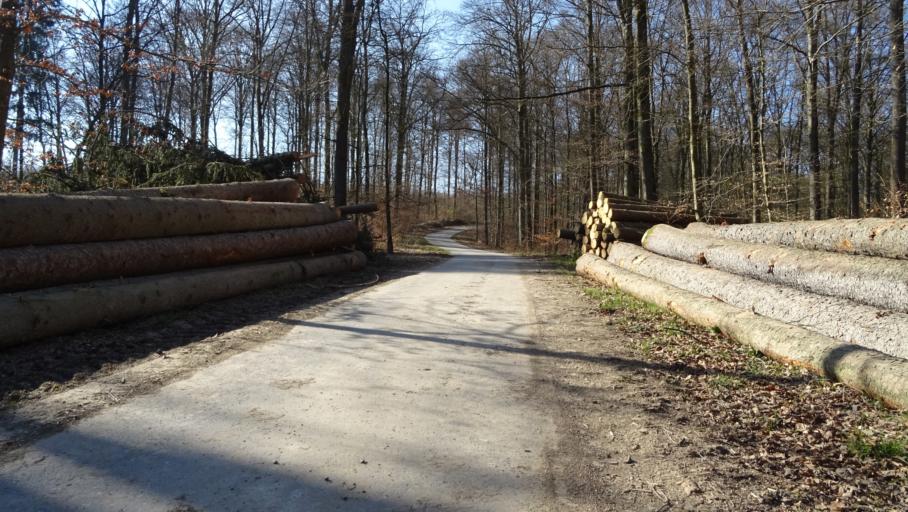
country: DE
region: Baden-Wuerttemberg
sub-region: Regierungsbezirk Stuttgart
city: Roigheim
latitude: 49.3910
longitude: 9.3225
